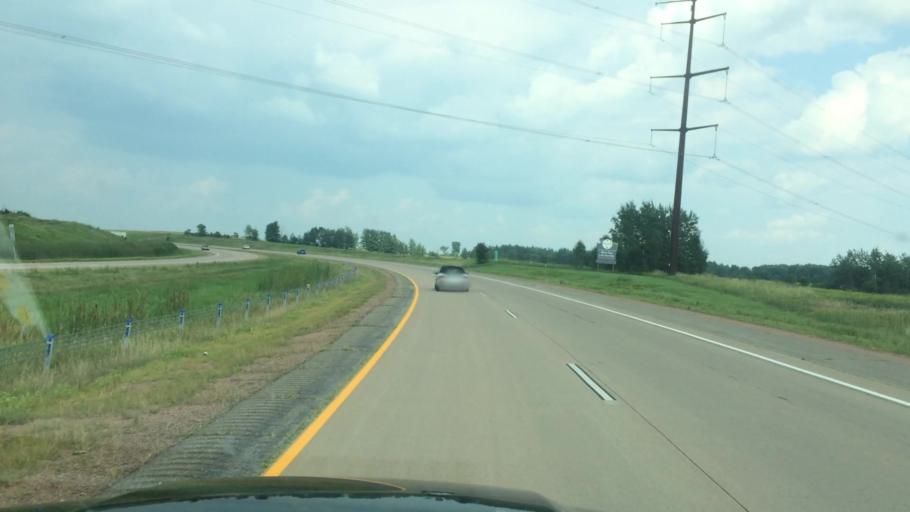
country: US
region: Wisconsin
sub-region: Clark County
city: Abbotsford
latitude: 44.9341
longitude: -90.2953
